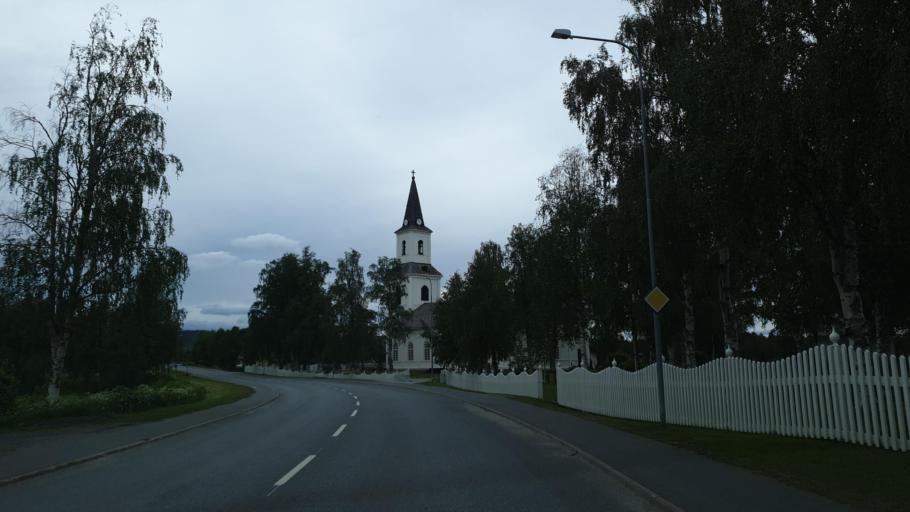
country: SE
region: Vaesterbotten
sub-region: Sorsele Kommun
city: Sorsele
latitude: 65.5411
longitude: 17.5173
